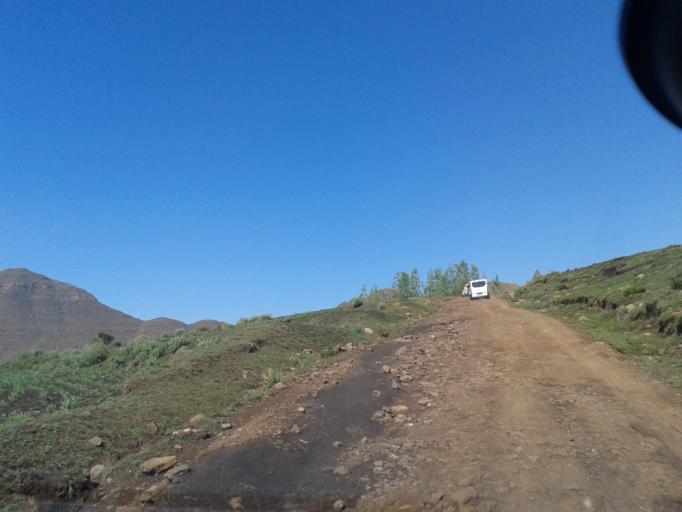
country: LS
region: Maseru
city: Nako
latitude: -29.8443
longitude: 27.5625
